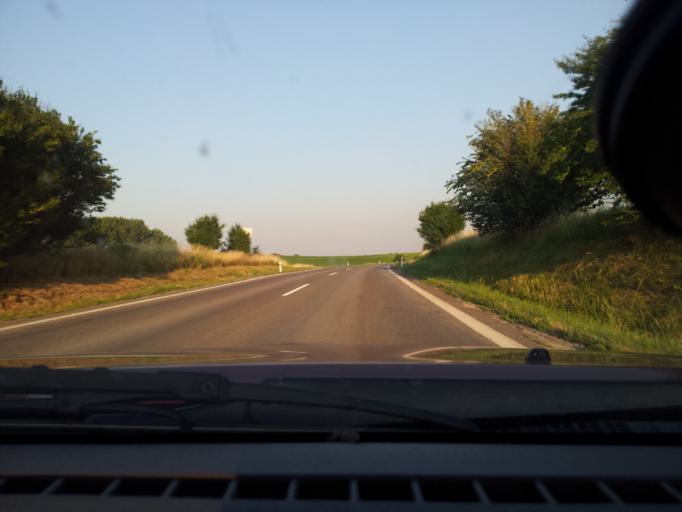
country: SK
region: Trnavsky
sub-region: Okres Senica
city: Senica
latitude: 48.7566
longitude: 17.3174
